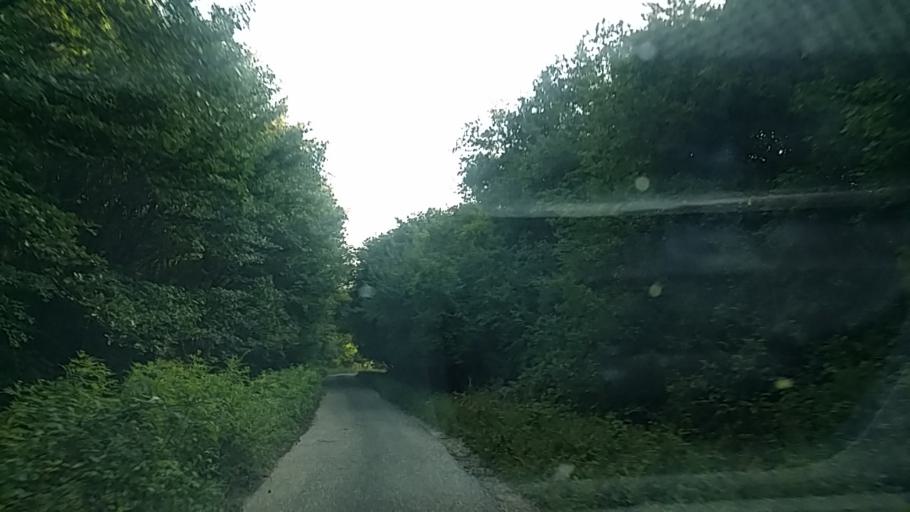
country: HU
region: Komarom-Esztergom
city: Tatabanya
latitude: 47.5928
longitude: 18.4256
